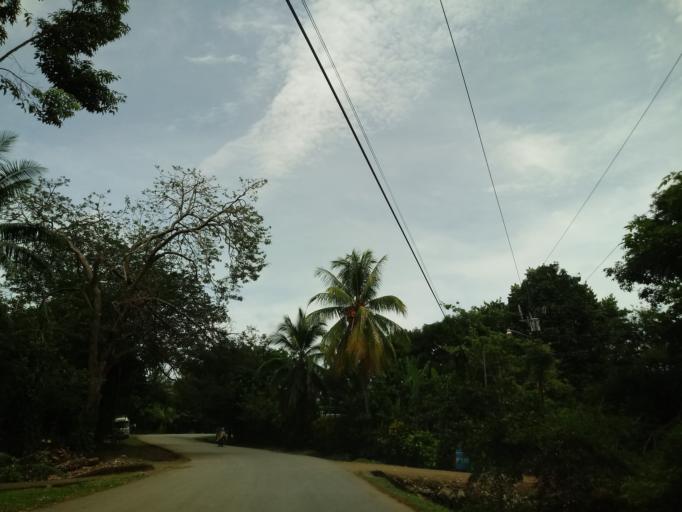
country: CR
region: San Jose
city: Daniel Flores
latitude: 9.1572
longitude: -83.7456
